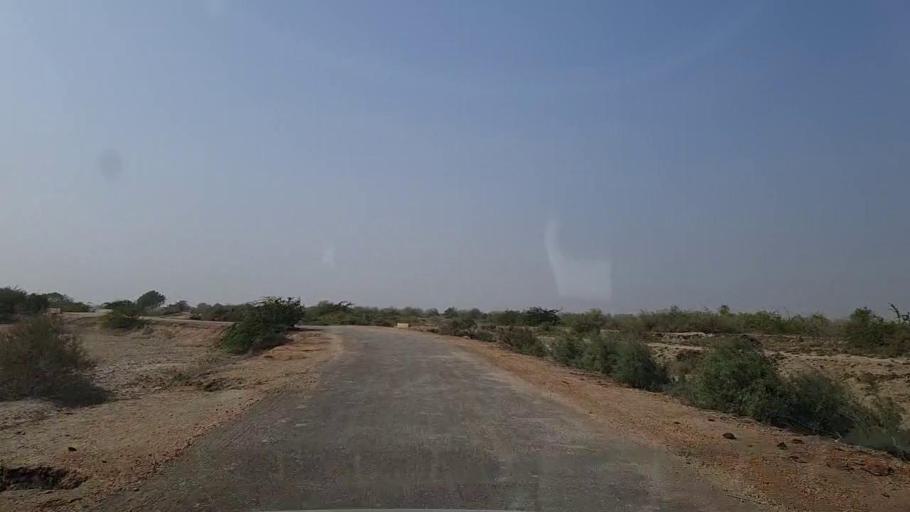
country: PK
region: Sindh
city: Mirpur Sakro
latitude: 24.5300
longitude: 67.5590
